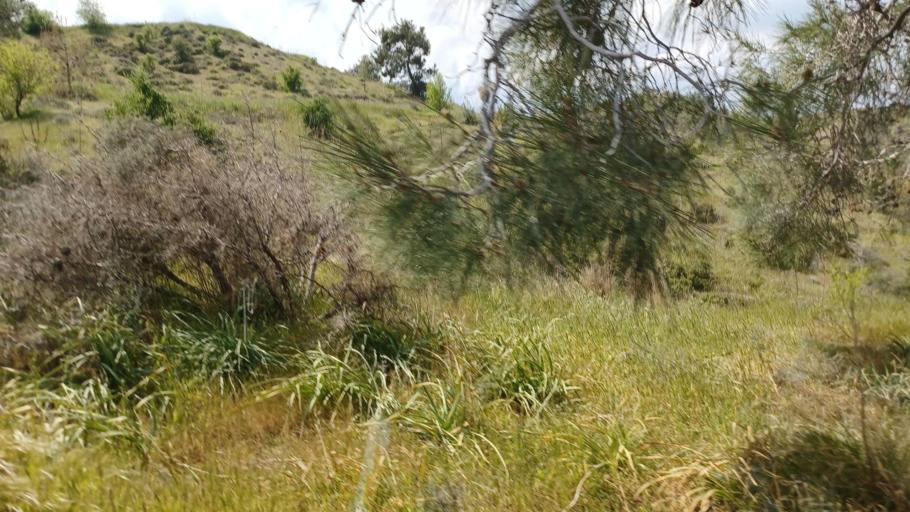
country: CY
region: Lefkosia
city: Kakopetria
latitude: 35.0763
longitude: 32.9434
